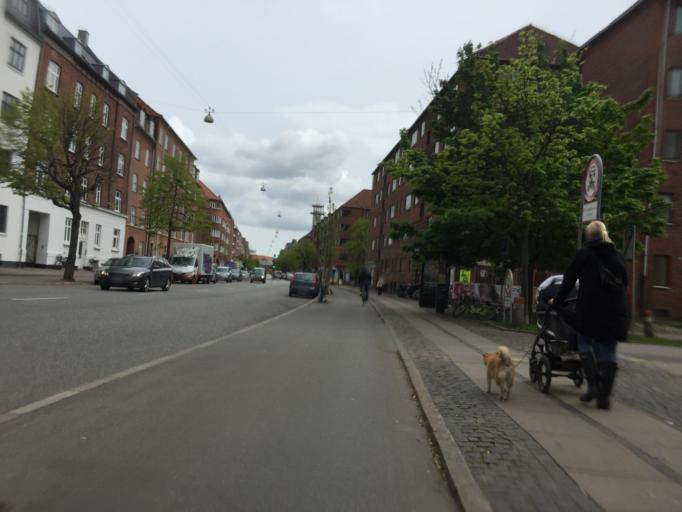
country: DK
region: Capital Region
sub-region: Frederiksberg Kommune
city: Frederiksberg
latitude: 55.6949
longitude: 12.5287
